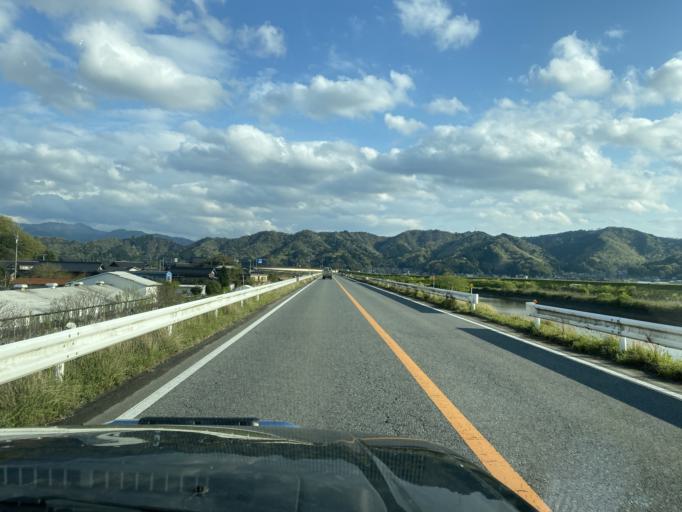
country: JP
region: Hyogo
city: Toyooka
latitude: 35.4962
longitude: 134.8405
